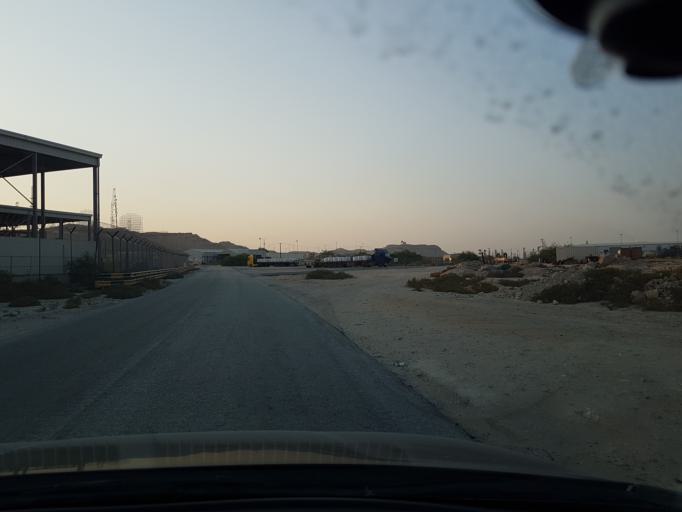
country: BH
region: Central Governorate
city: Dar Kulayb
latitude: 26.0248
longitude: 50.5557
